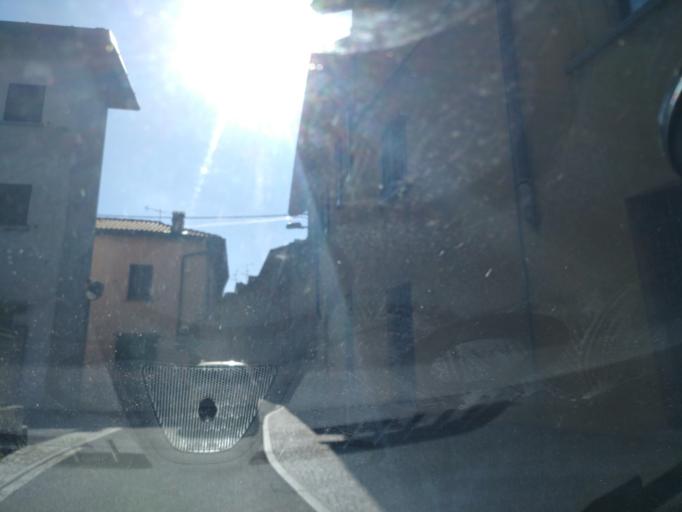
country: IT
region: Lombardy
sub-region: Provincia di Como
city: Montorfano
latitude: 45.7855
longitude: 9.1446
